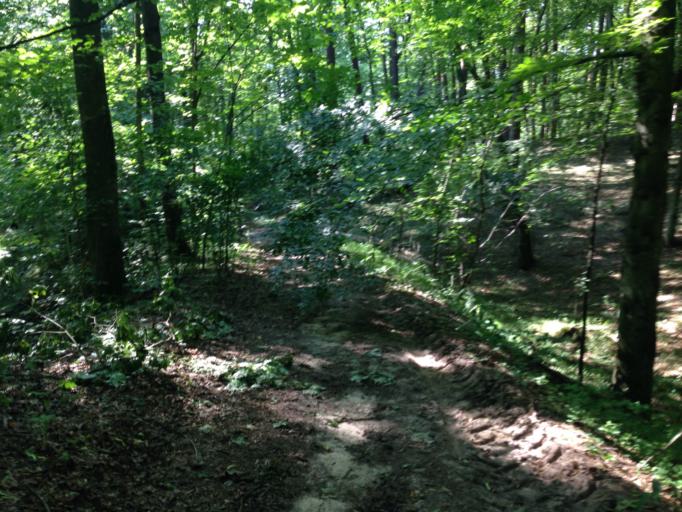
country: PL
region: Kujawsko-Pomorskie
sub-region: Powiat brodnicki
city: Gorzno
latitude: 53.1841
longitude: 19.6591
